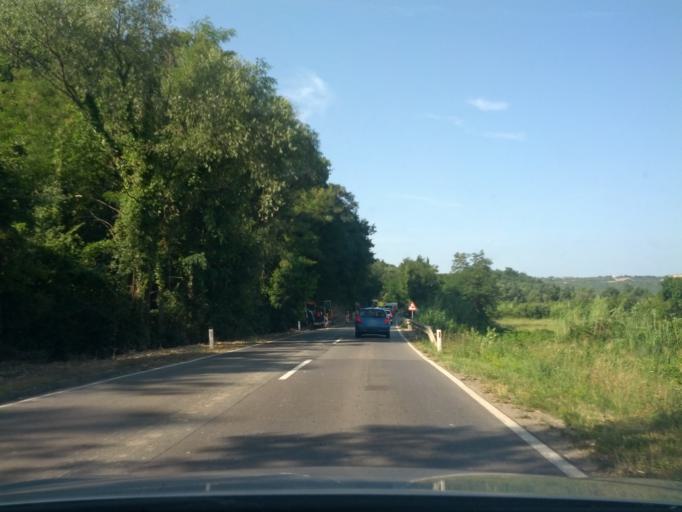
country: HR
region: Istarska
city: Buje
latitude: 45.4699
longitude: 13.6711
